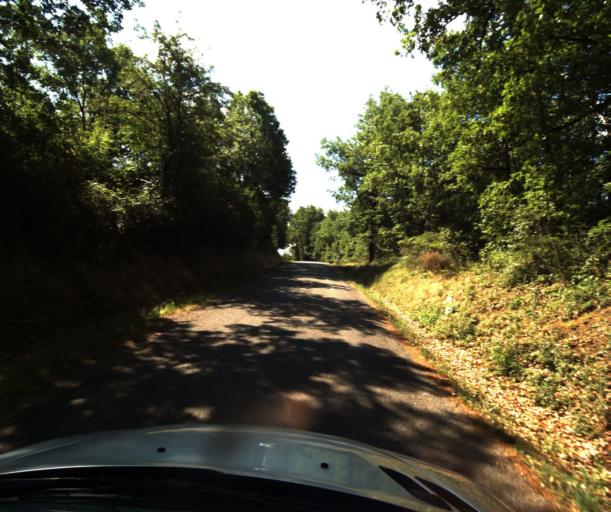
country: FR
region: Midi-Pyrenees
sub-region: Departement du Tarn-et-Garonne
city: Finhan
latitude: 43.8985
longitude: 1.2717
